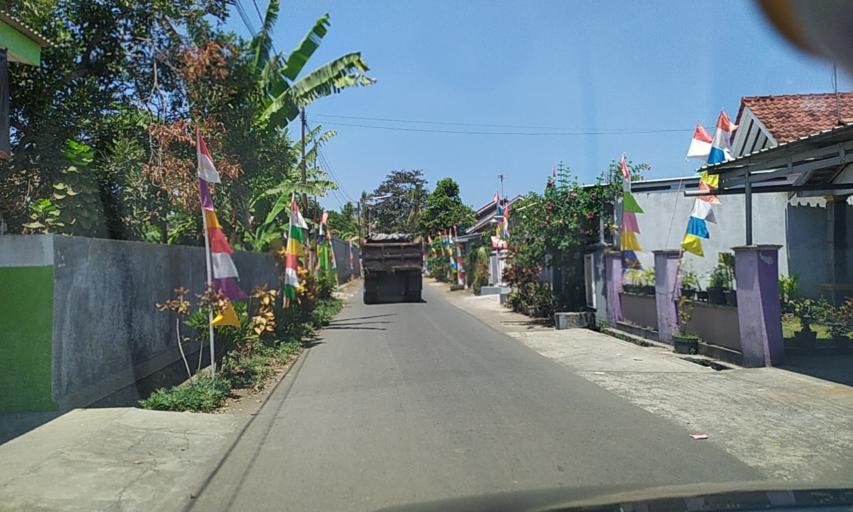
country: ID
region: Central Java
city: Rejanegara
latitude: -7.6767
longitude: 109.0625
